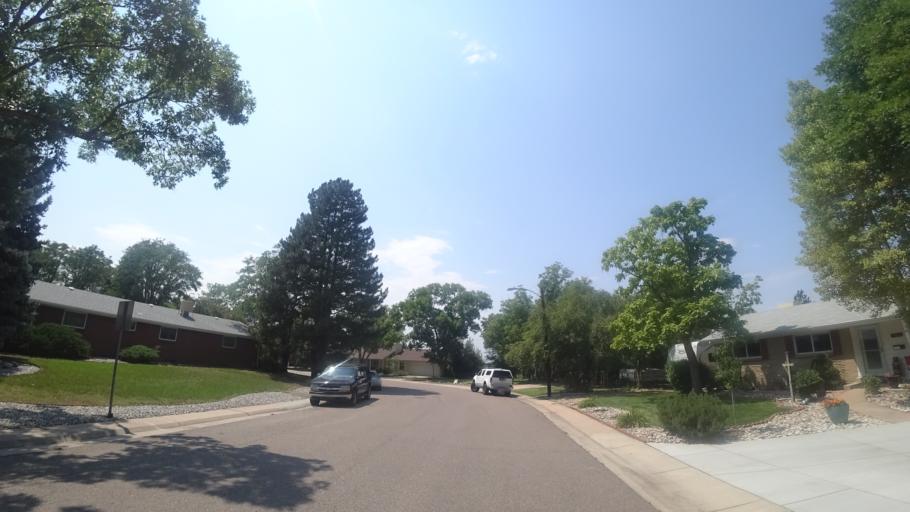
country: US
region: Colorado
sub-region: Arapahoe County
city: Littleton
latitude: 39.6120
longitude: -104.9845
